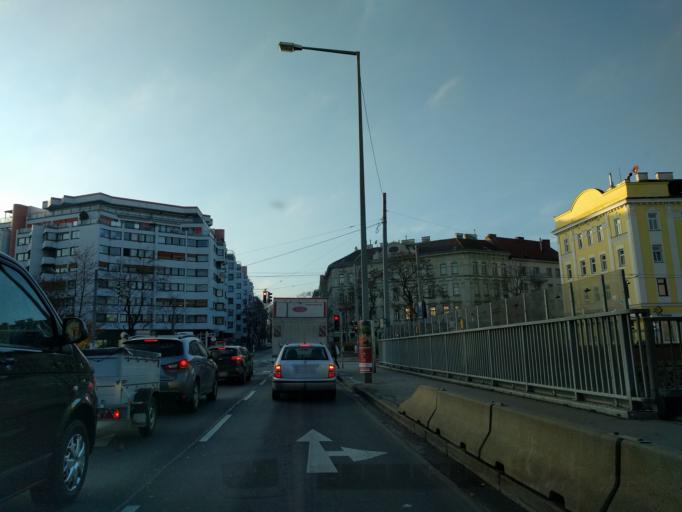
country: AT
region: Vienna
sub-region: Wien Stadt
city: Vienna
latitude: 48.2077
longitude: 16.3100
